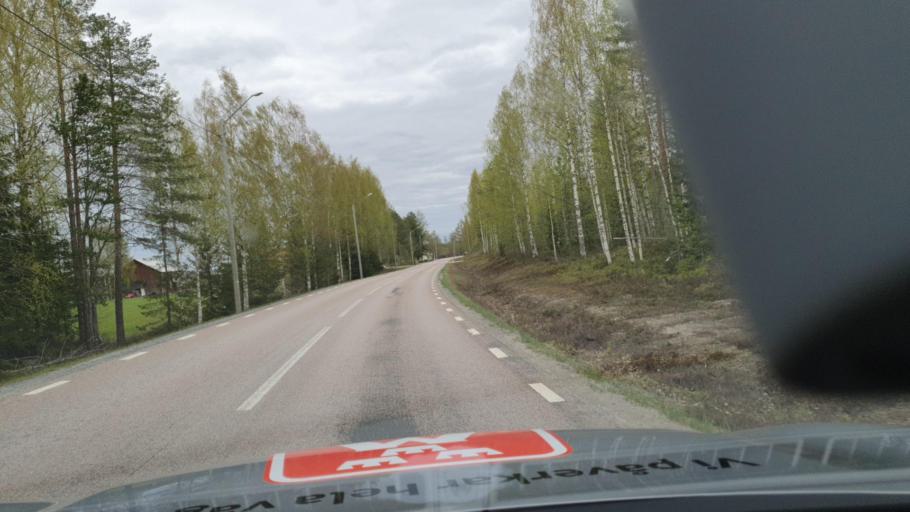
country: SE
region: Vaesternorrland
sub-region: OErnskoeldsviks Kommun
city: Husum
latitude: 63.4779
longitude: 18.9502
